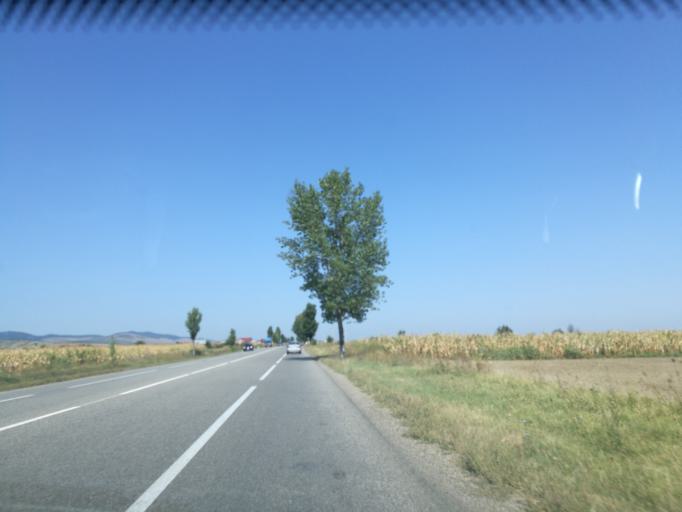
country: RO
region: Bacau
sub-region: Comuna Faraoani
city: Faraoani
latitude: 46.4296
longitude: 26.9269
